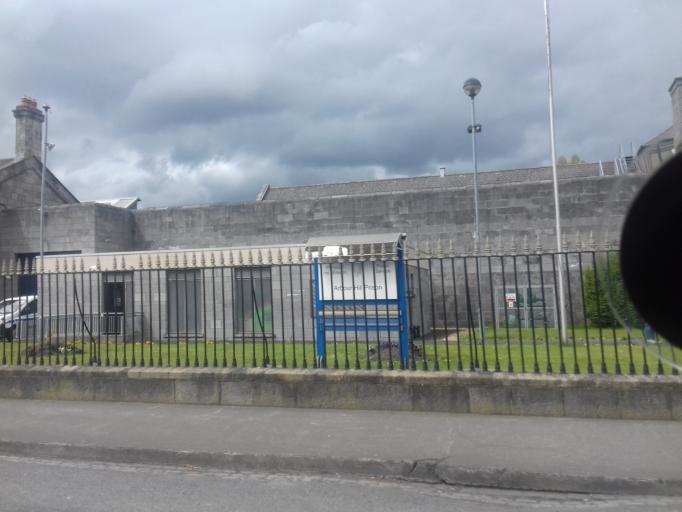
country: IE
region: Leinster
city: Rialto
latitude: 53.3496
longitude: -6.2880
